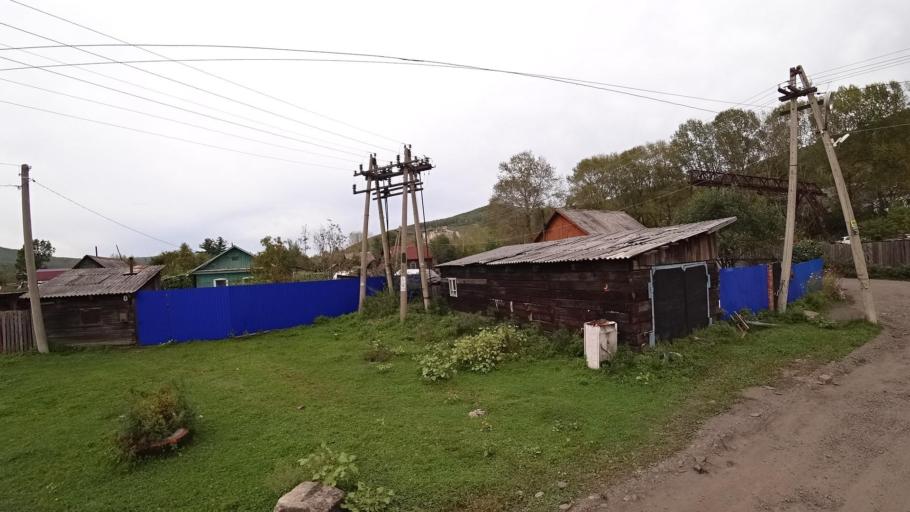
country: RU
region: Jewish Autonomous Oblast
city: Khingansk
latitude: 49.0334
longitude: 131.0561
